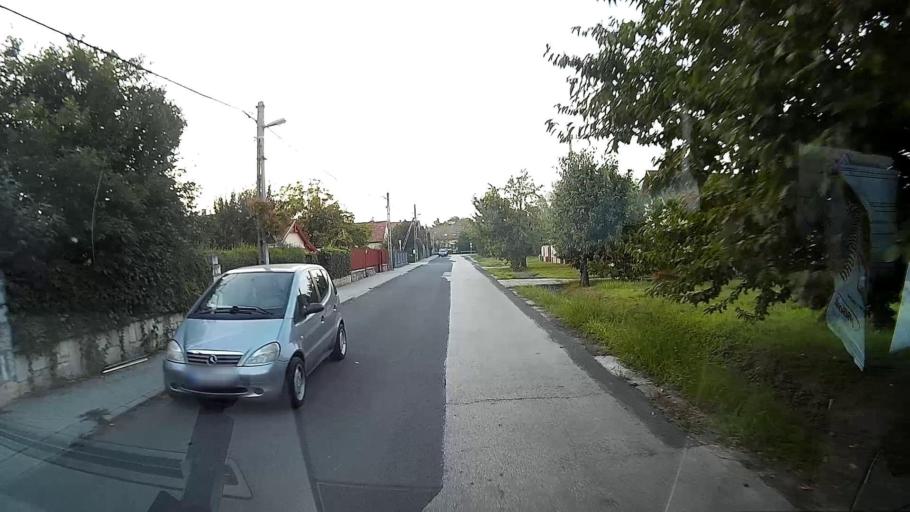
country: HU
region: Pest
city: Budakalasz
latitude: 47.6280
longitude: 19.0519
